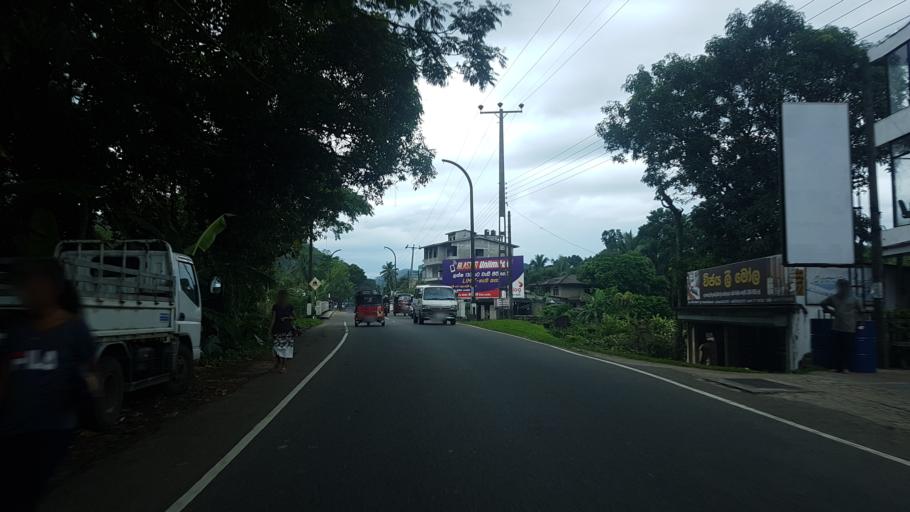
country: LK
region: Western
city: Hanwella Ihala
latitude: 7.0334
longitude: 80.2937
